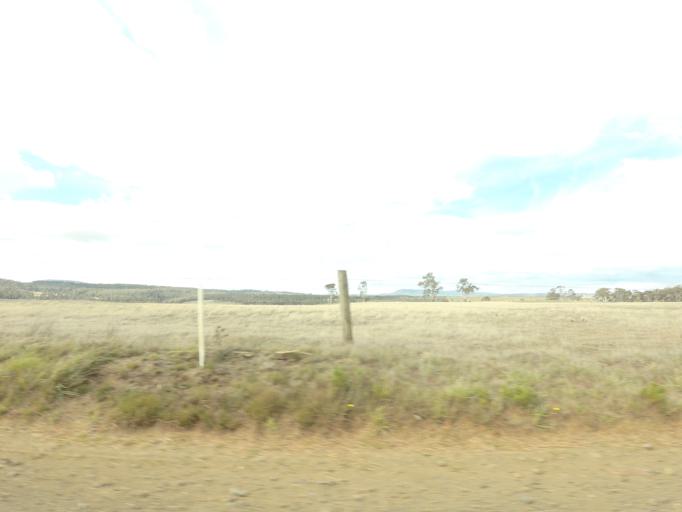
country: AU
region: Tasmania
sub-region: Brighton
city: Bridgewater
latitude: -42.4342
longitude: 147.3860
